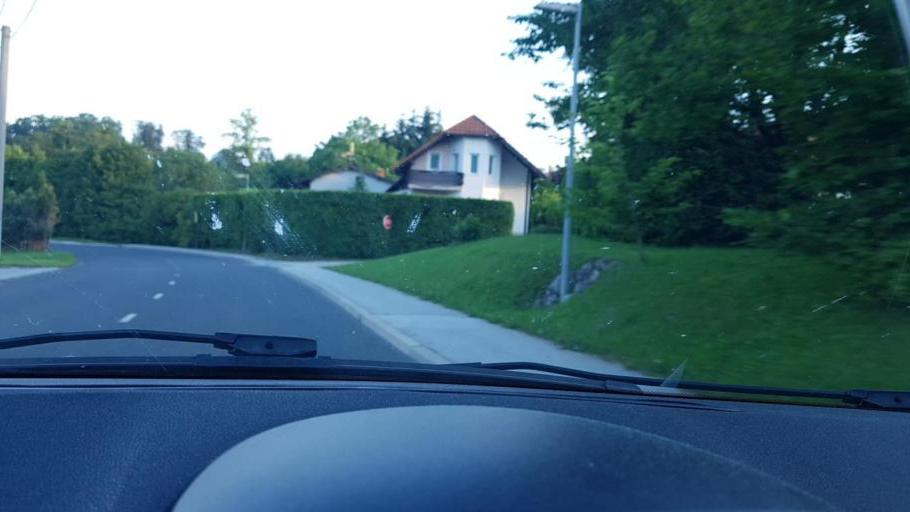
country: SI
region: Rogaska Slatina
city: Rogaska Slatina
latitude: 46.2518
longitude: 15.6210
